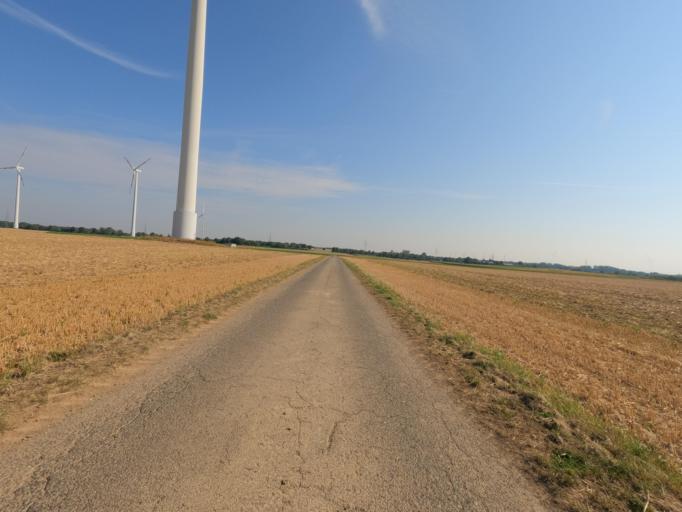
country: DE
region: North Rhine-Westphalia
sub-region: Regierungsbezirk Koln
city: Aldenhoven
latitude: 50.9272
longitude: 6.2782
